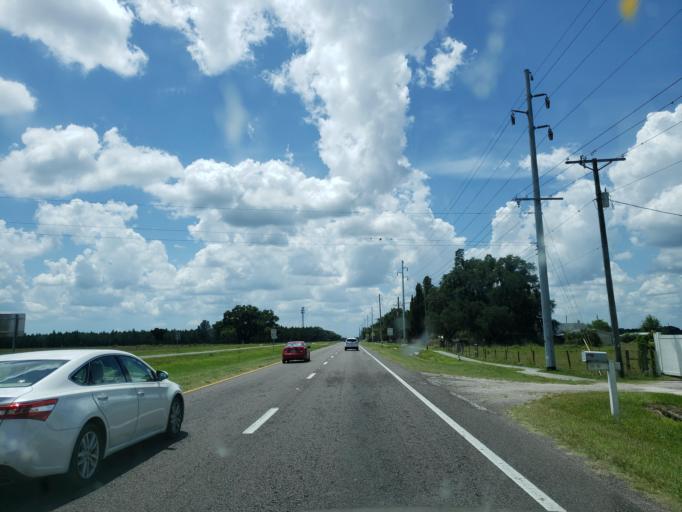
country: US
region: Florida
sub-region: Hillsborough County
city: Plant City
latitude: 27.9378
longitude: -82.1248
